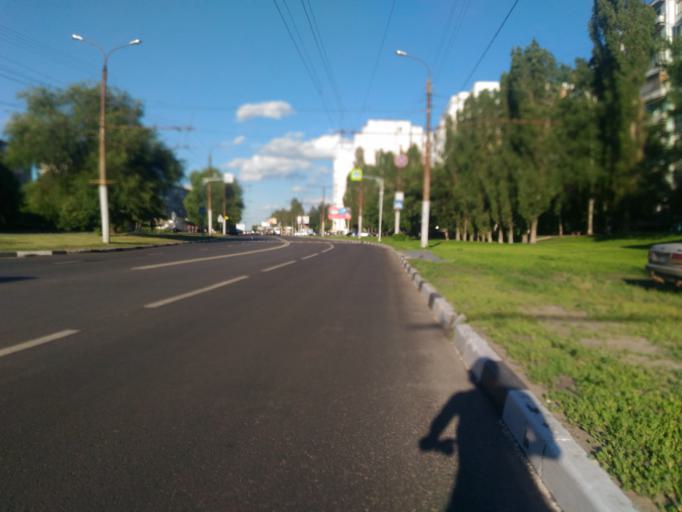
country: RU
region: Voronezj
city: Pridonskoy
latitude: 51.6537
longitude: 39.1172
